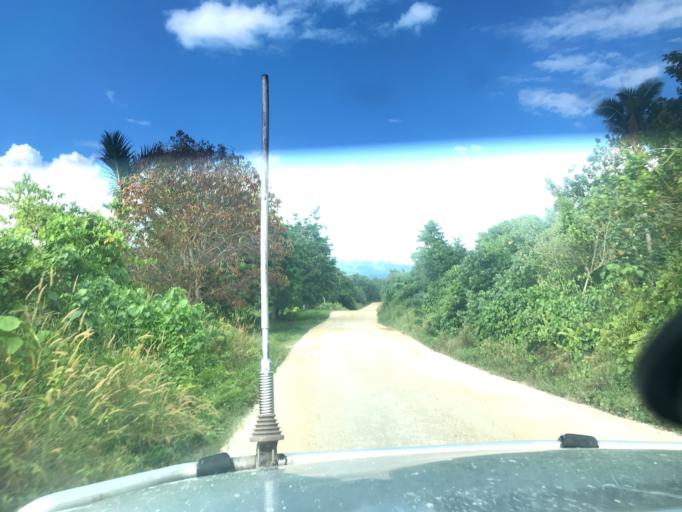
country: SB
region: Malaita
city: Auki
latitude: -8.5743
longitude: 160.6932
